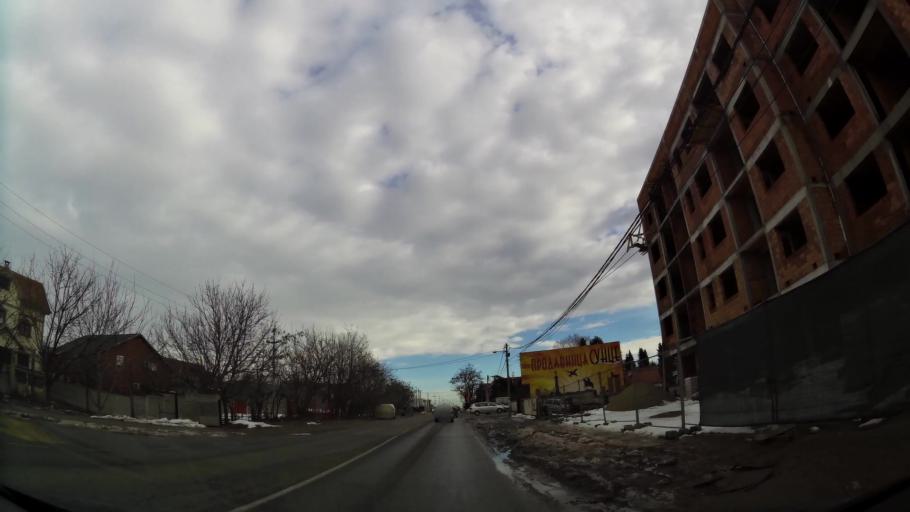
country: RS
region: Central Serbia
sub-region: Belgrade
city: Surcin
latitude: 44.8011
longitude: 20.3356
